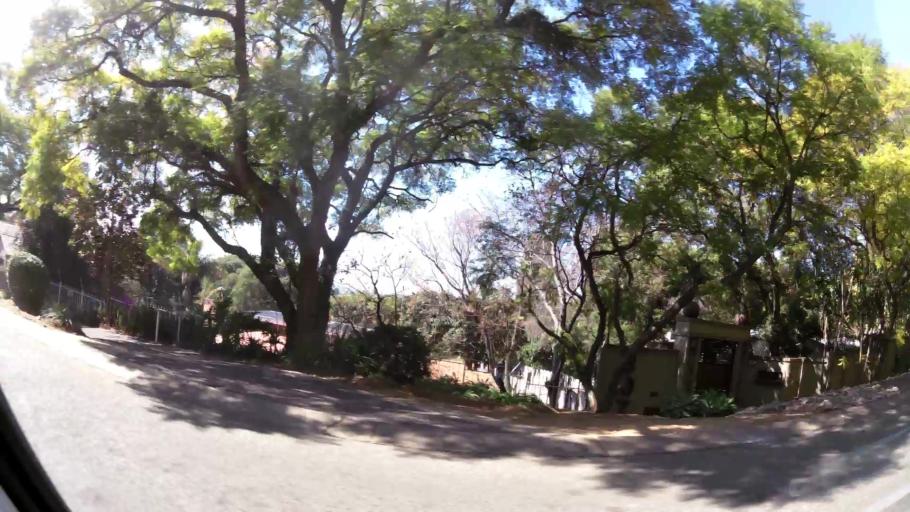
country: ZA
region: Gauteng
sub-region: City of Tshwane Metropolitan Municipality
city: Pretoria
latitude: -25.7913
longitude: 28.2407
